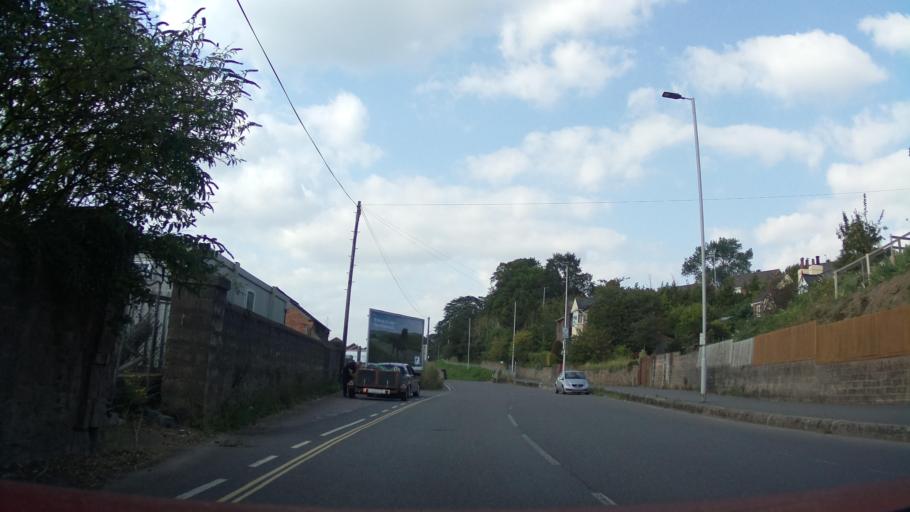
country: GB
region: England
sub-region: Devon
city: Exeter
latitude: 50.7332
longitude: -3.5436
